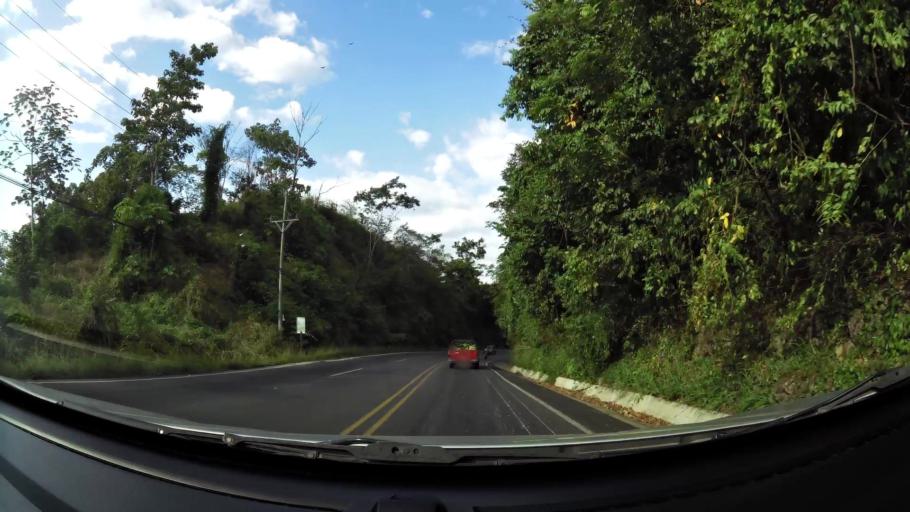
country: CR
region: Puntarenas
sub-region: Canton de Garabito
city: Jaco
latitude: 9.6937
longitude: -84.6414
